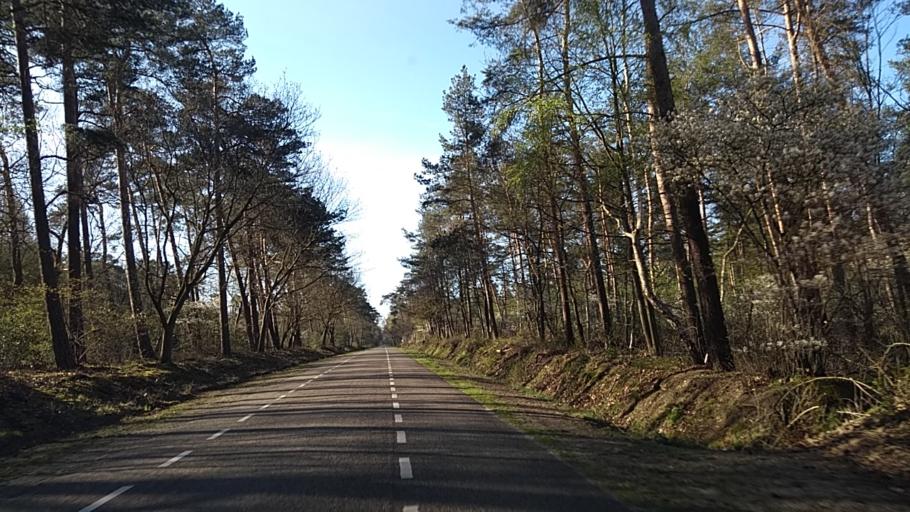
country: NL
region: Overijssel
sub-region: Gemeente Hof van Twente
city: Delden
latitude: 52.2766
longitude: 6.6689
